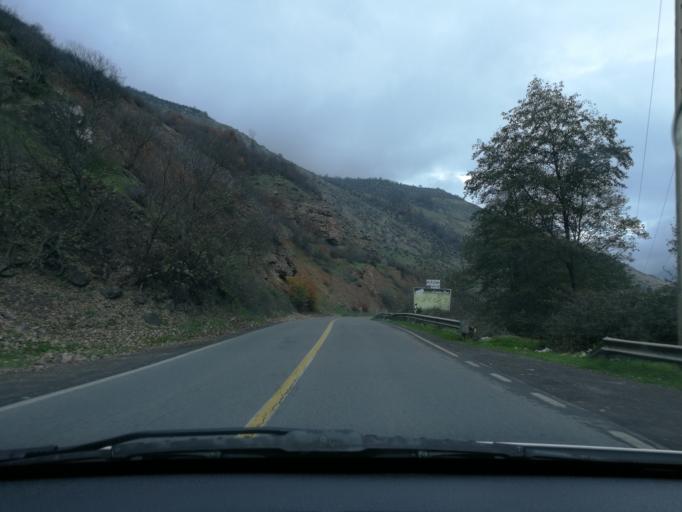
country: IR
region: Mazandaran
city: Chalus
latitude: 36.3645
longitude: 51.2615
